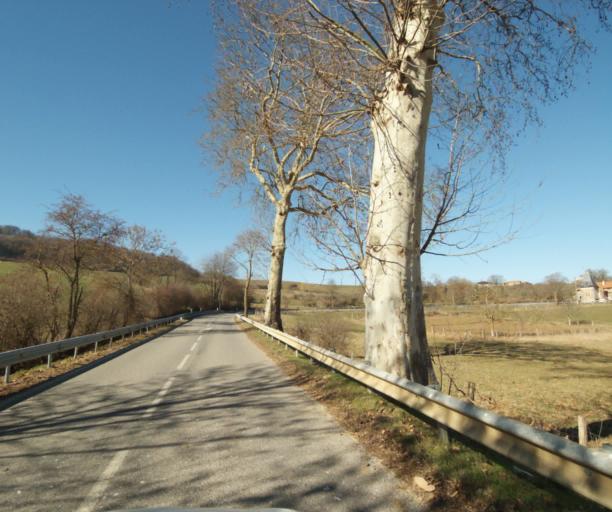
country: FR
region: Lorraine
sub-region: Departement de Meurthe-et-Moselle
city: Essey-les-Nancy
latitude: 48.7153
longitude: 6.2388
